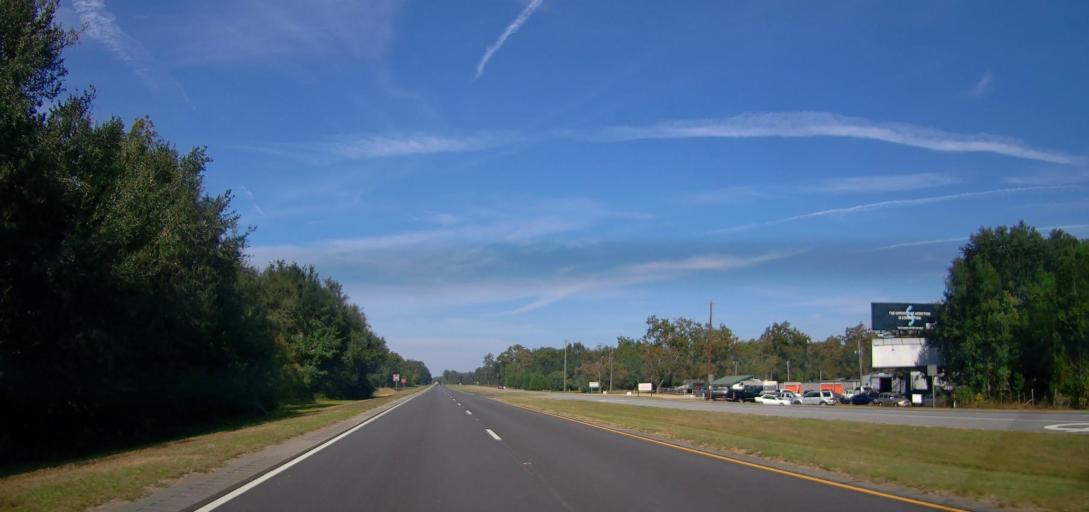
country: US
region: Georgia
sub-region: Dougherty County
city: Putney
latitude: 31.3837
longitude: -84.1492
